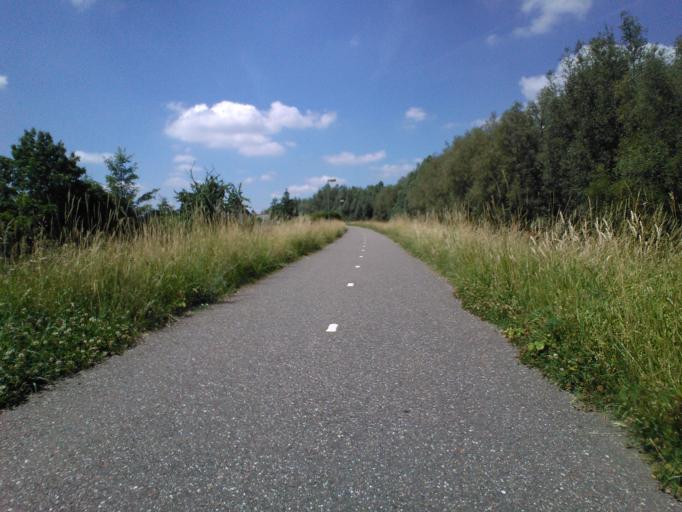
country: NL
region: South Holland
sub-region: Gemeente Gorinchem
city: Gorinchem
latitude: 51.8205
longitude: 4.9547
